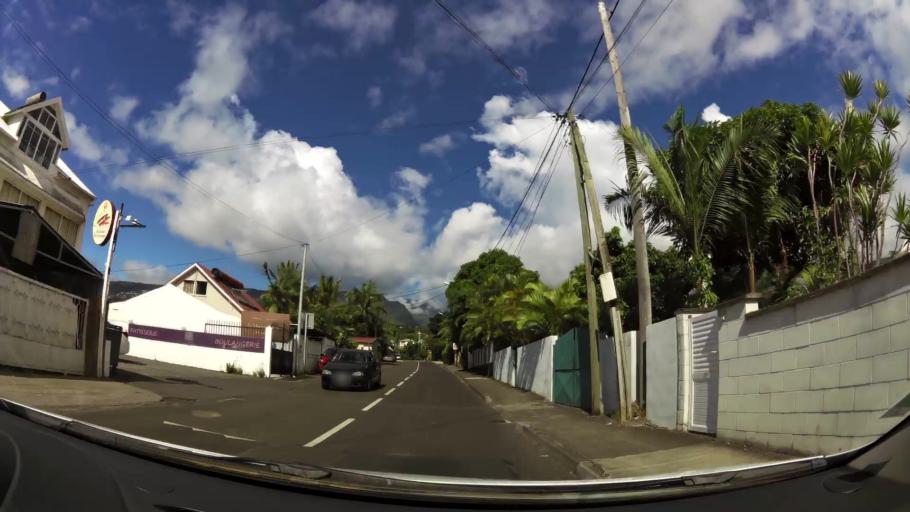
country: RE
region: Reunion
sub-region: Reunion
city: Saint-Denis
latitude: -20.9207
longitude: 55.4945
